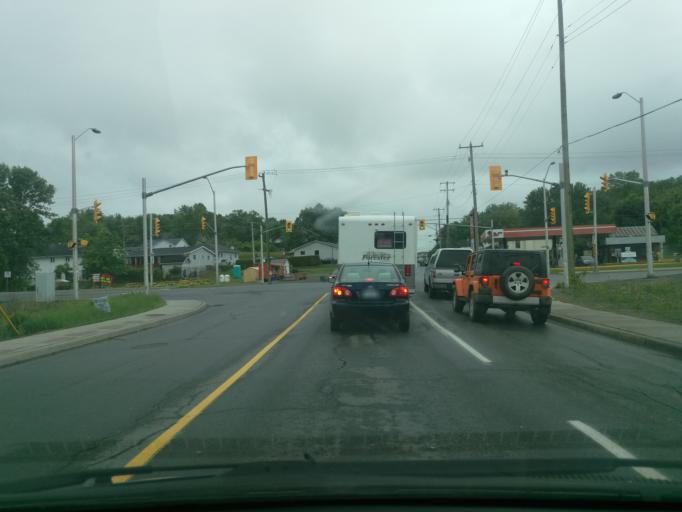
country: CA
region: Ontario
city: Clarence-Rockland
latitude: 45.5506
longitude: -75.2952
